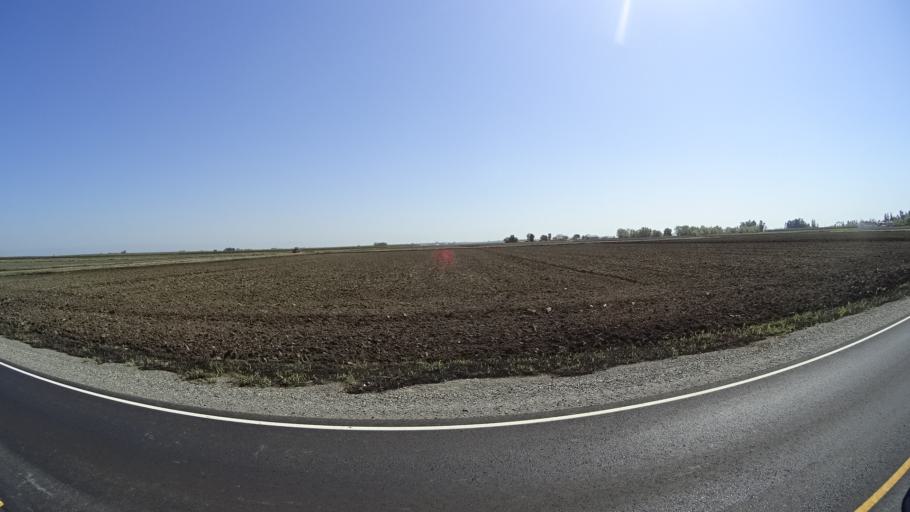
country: US
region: California
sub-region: Glenn County
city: Hamilton City
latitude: 39.6085
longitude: -122.0656
